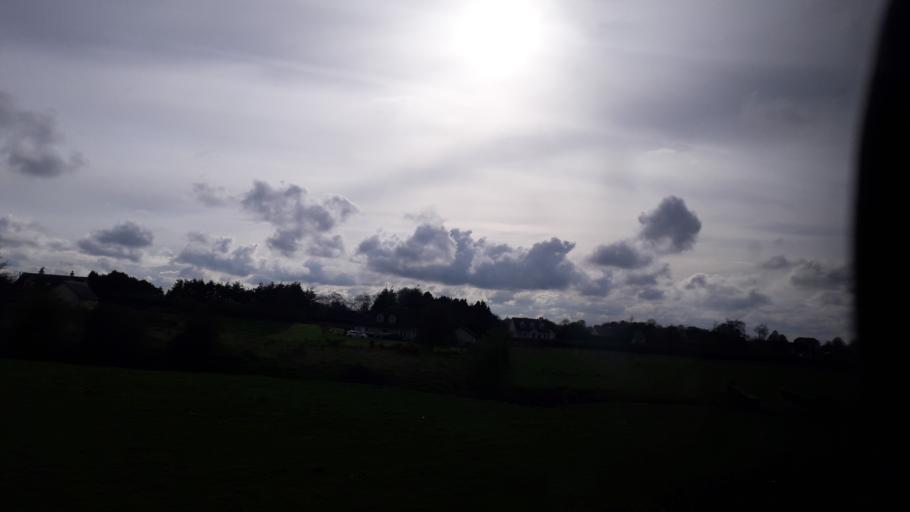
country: IE
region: Leinster
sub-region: An Mhi
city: Enfield
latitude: 53.4165
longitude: -6.8837
